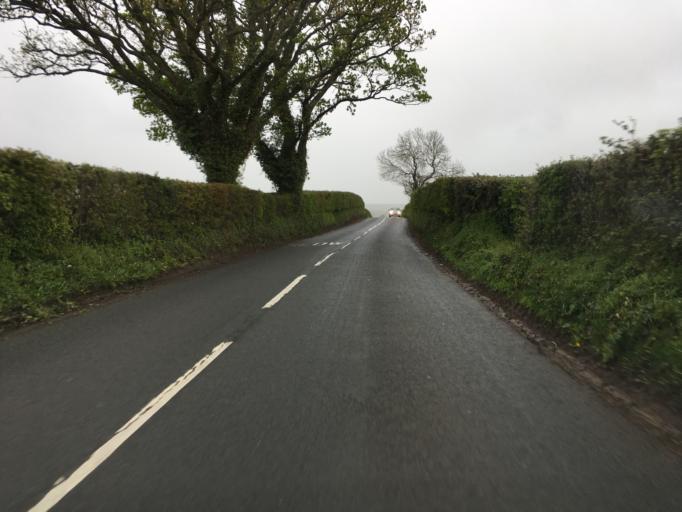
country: GB
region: England
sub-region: Bath and North East Somerset
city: East Harptree
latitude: 51.3134
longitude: -2.6282
